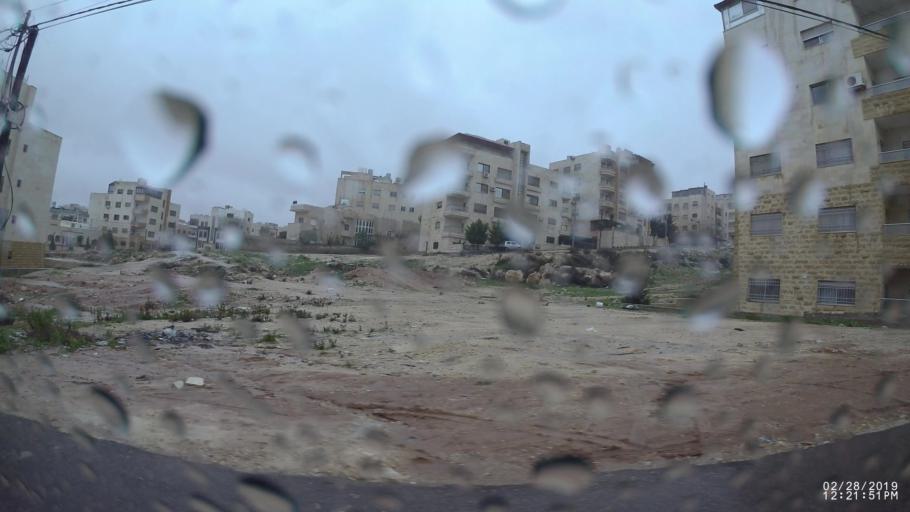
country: JO
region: Amman
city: Al Jubayhah
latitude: 32.0268
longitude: 35.8877
